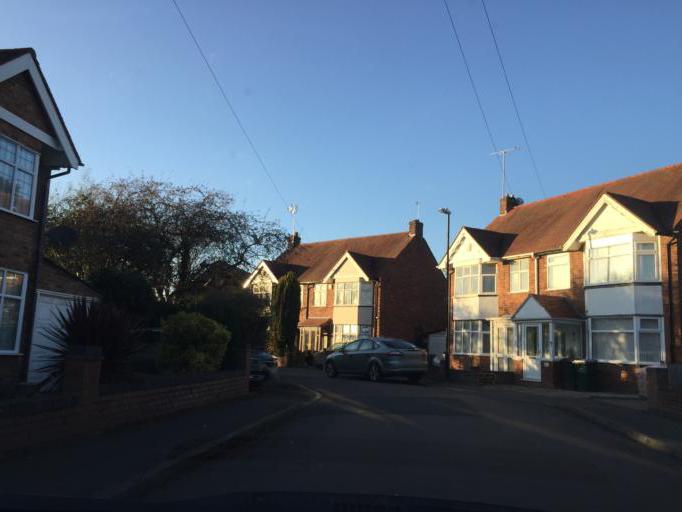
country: GB
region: England
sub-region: Warwickshire
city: Ryton on Dunsmore
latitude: 52.4022
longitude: -1.4566
